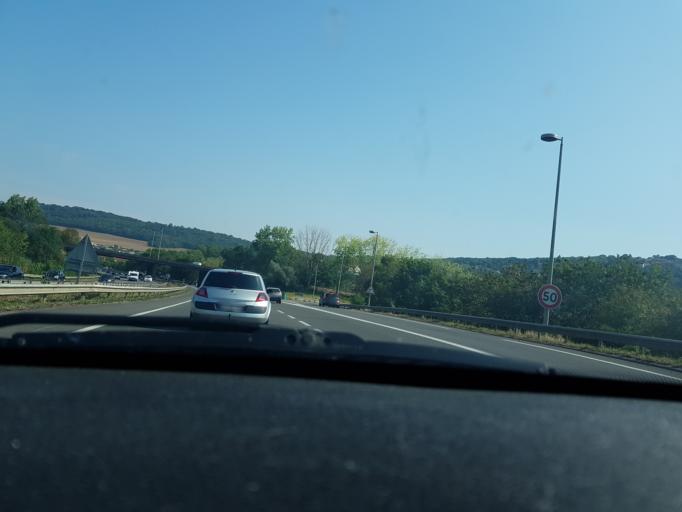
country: FR
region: Lorraine
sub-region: Departement de Meurthe-et-Moselle
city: Bouxieres-aux-Dames
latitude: 48.7495
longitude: 6.1568
